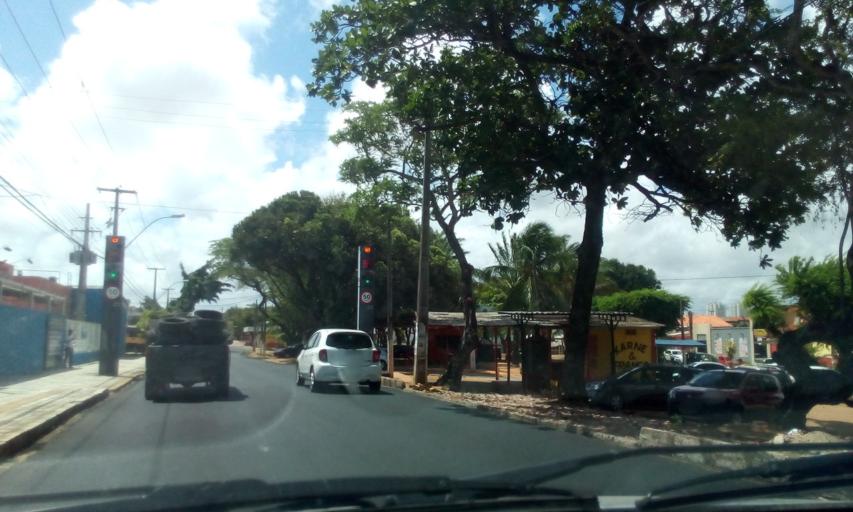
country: BR
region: Rio Grande do Norte
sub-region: Natal
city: Natal
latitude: -5.8567
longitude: -35.2058
